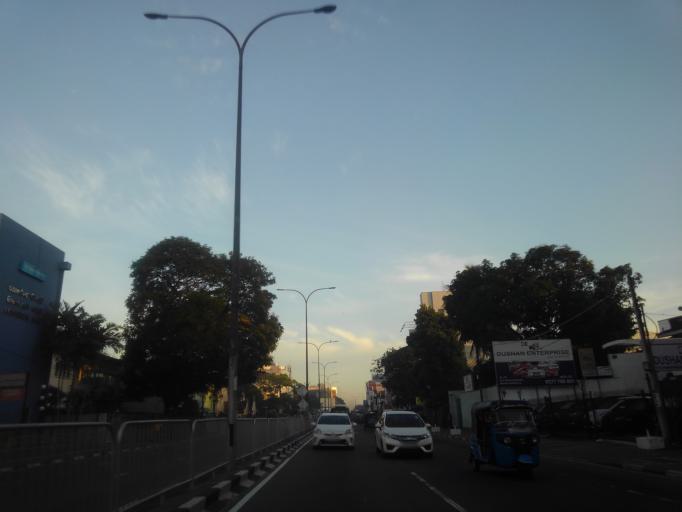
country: LK
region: Western
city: Kolonnawa
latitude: 6.9116
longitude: 79.8775
